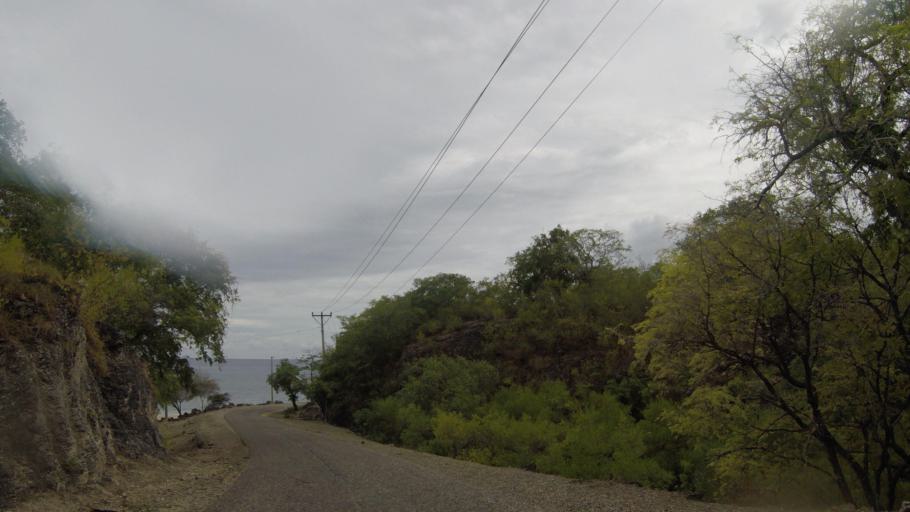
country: TL
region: Lautem
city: Lospalos
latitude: -8.3448
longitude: 127.0469
